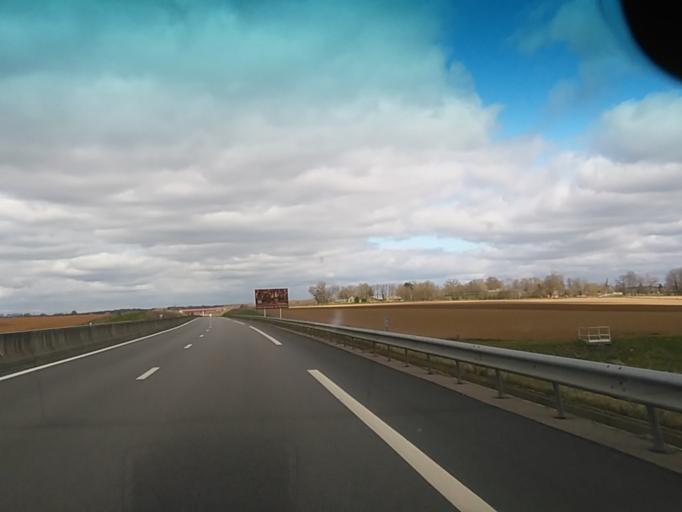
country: FR
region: Haute-Normandie
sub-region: Departement de l'Eure
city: Bourg-Achard
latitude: 49.3163
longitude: 0.8210
